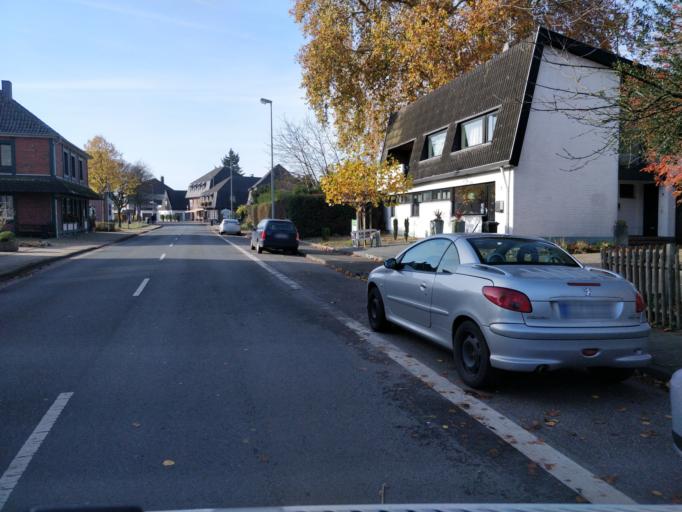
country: DE
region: North Rhine-Westphalia
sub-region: Regierungsbezirk Munster
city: Isselburg
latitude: 51.7766
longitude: 6.4605
